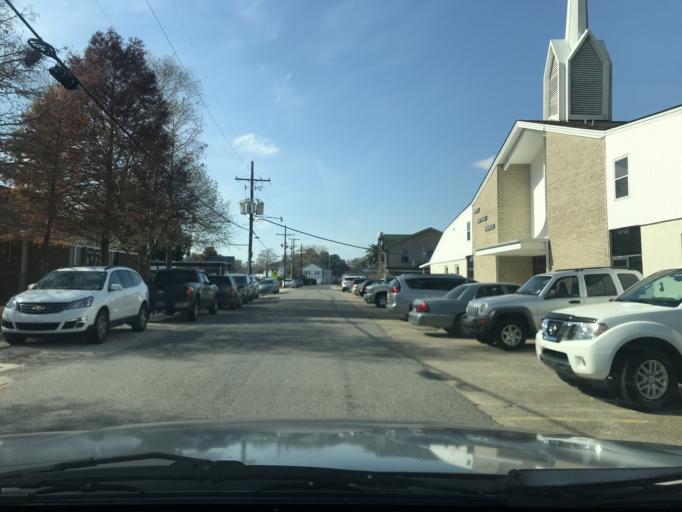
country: US
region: Louisiana
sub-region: Jefferson Parish
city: Marrero
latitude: 29.9001
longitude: -90.0910
